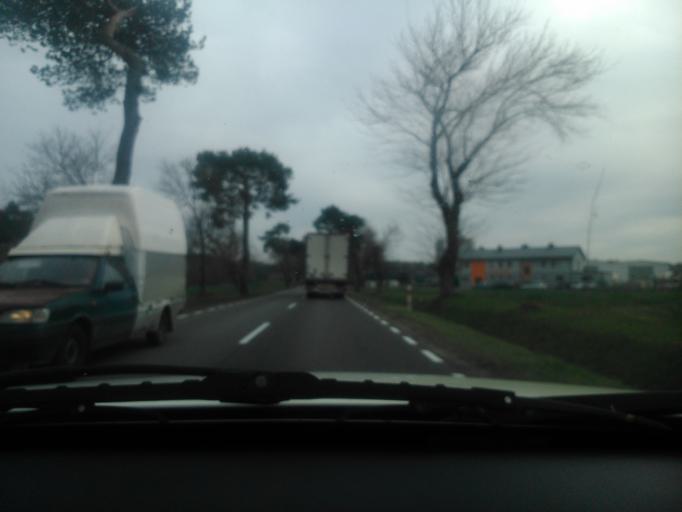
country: PL
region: Masovian Voivodeship
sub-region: Powiat mlawski
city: Szydlowo
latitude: 53.0790
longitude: 20.4711
